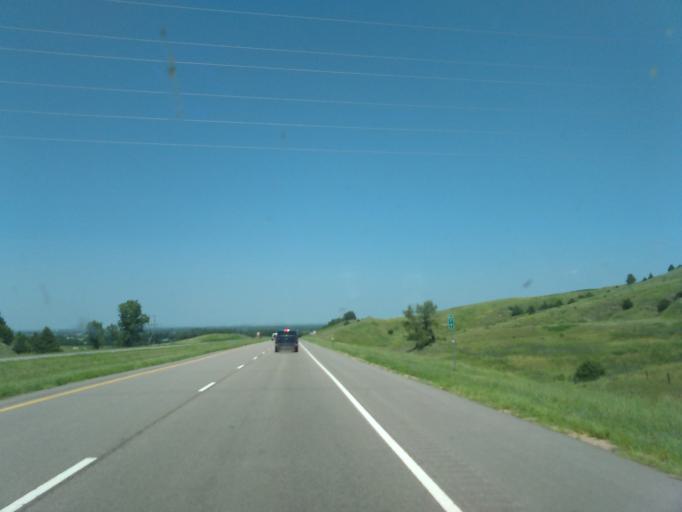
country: US
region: Nebraska
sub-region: Lincoln County
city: North Platte
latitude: 41.0752
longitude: -100.7626
